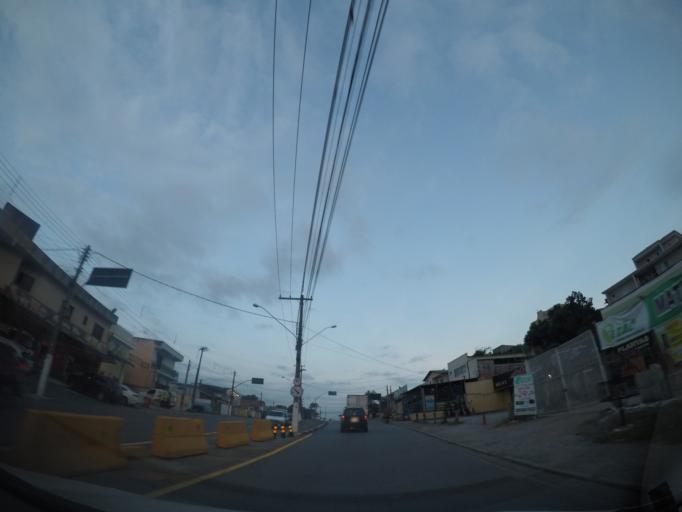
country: BR
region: Sao Paulo
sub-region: Aruja
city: Aruja
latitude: -23.3884
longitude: -46.3141
